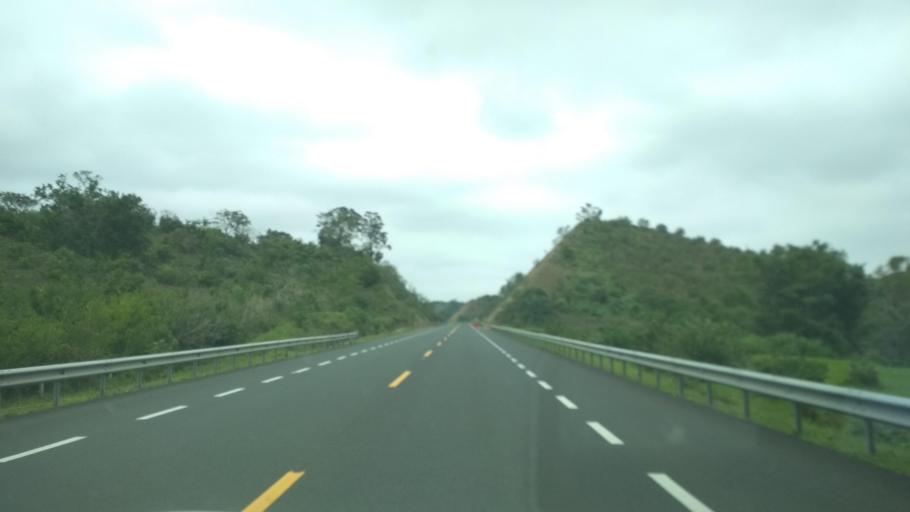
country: MX
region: Veracruz
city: Gutierrez Zamora
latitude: 20.2939
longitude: -97.0755
